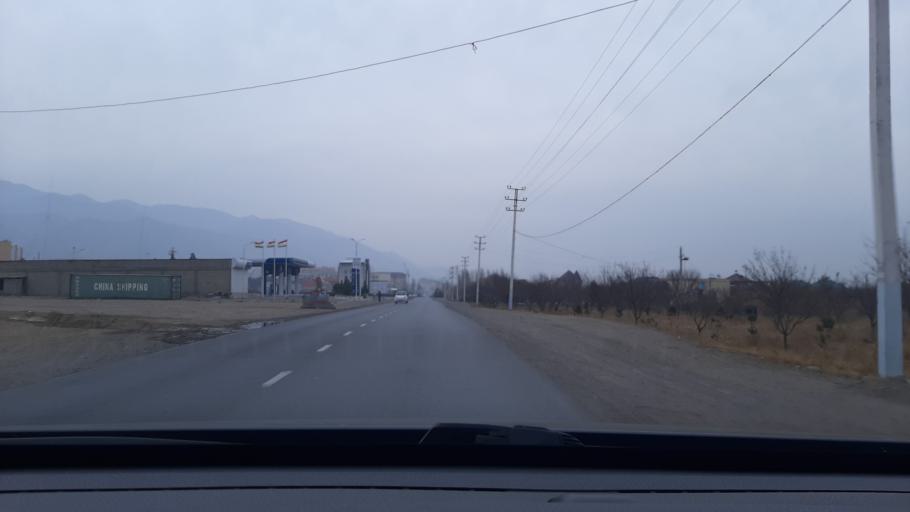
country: TJ
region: Viloyati Sughd
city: Khujand
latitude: 40.2761
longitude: 69.5800
